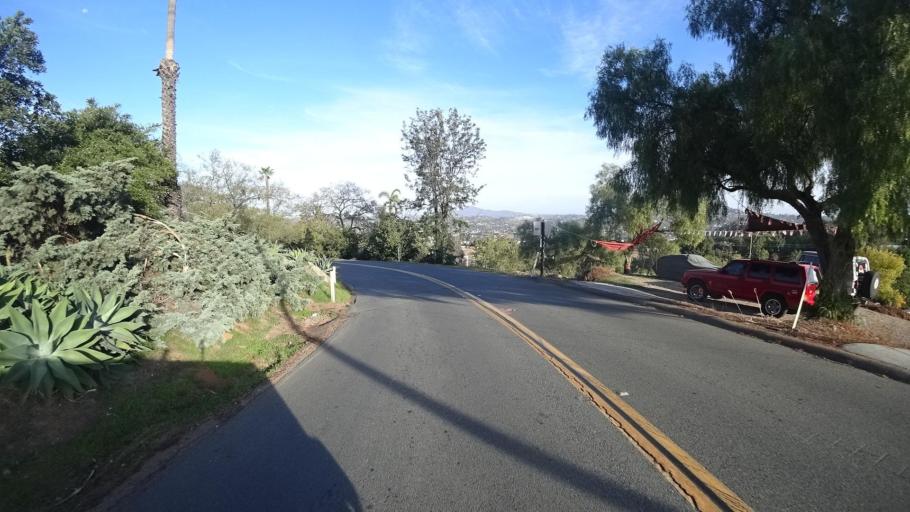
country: US
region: California
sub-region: San Diego County
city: Spring Valley
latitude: 32.7309
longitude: -116.9930
